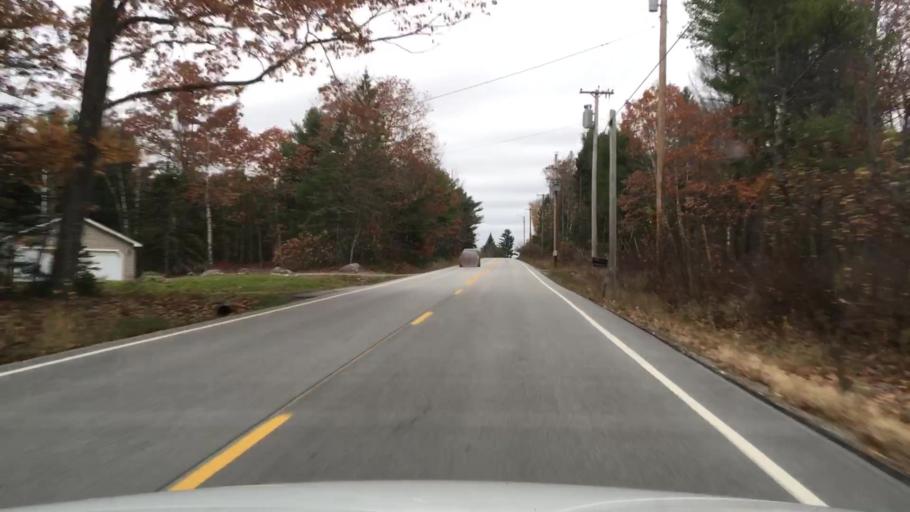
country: US
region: Maine
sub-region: Hancock County
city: Orland
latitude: 44.5442
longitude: -68.6865
